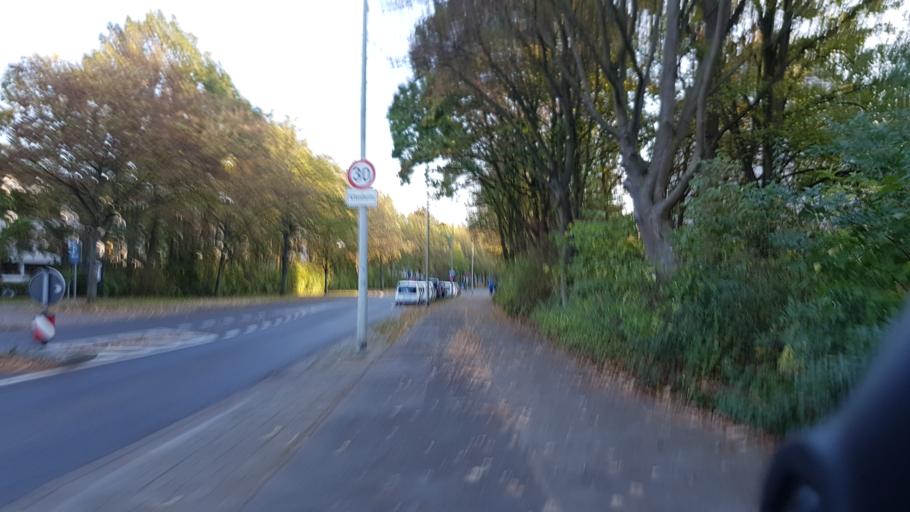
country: DE
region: Lower Saxony
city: Hemmingen
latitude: 52.3330
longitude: 9.7011
